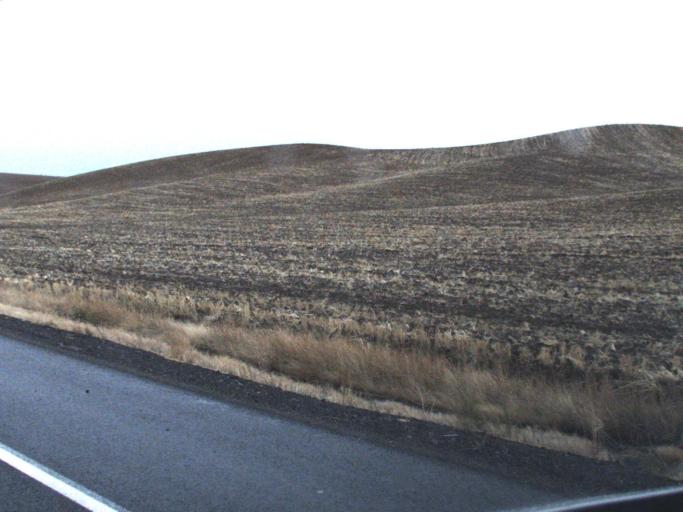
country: US
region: Washington
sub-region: Whitman County
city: Pullman
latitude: 46.7595
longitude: -117.2479
